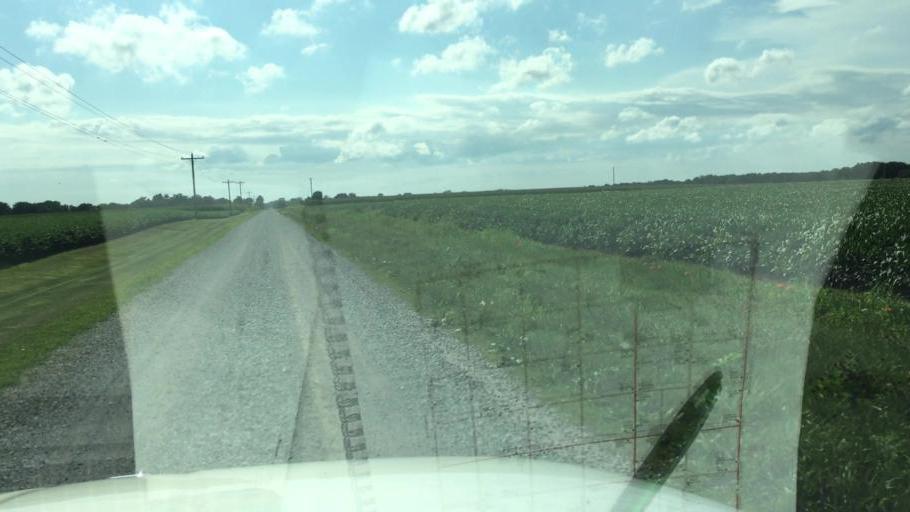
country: US
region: Illinois
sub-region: Hancock County
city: Nauvoo
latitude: 40.5216
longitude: -91.2951
